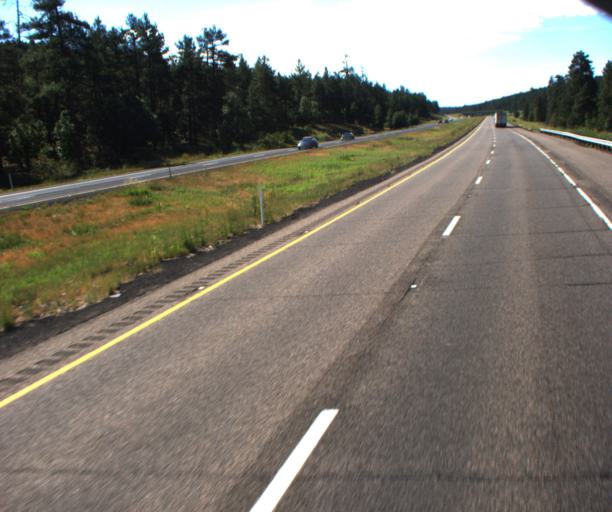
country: US
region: Arizona
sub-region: Coconino County
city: Sedona
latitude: 34.8835
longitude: -111.6403
